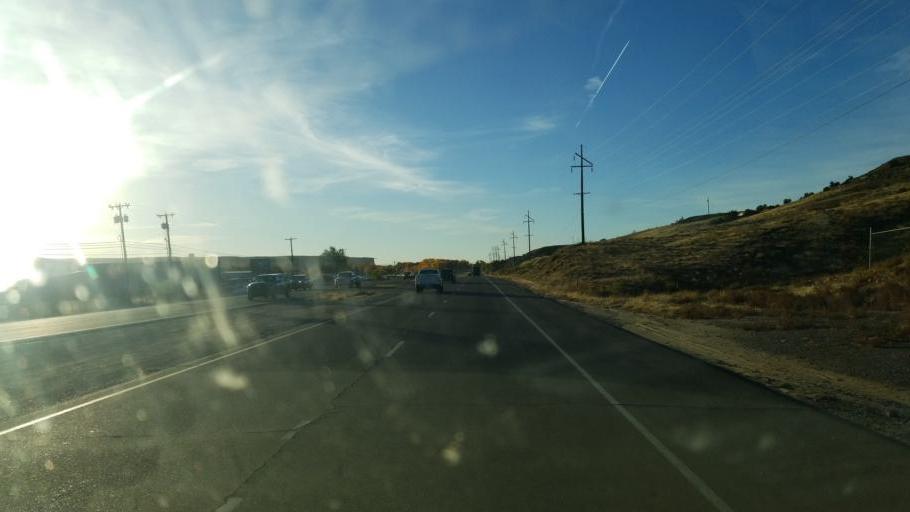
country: US
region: New Mexico
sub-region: San Juan County
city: Lee Acres
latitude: 36.7058
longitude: -108.1154
